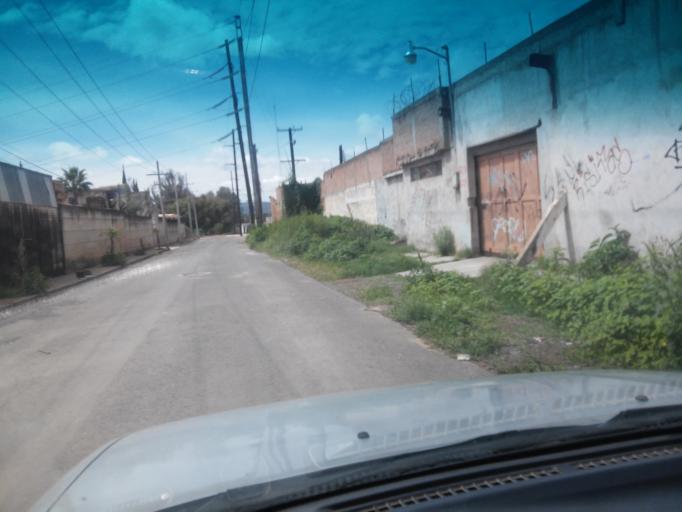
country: MX
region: Durango
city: Victoria de Durango
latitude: 24.0081
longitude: -104.6969
